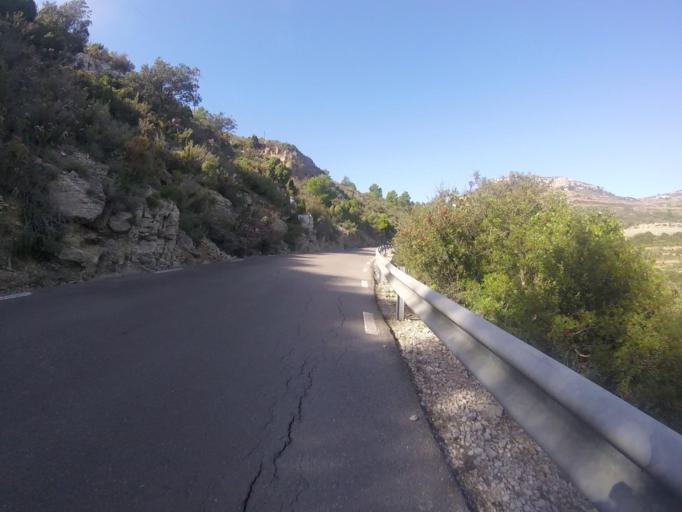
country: ES
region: Valencia
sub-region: Provincia de Castello
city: Sarratella
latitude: 40.2871
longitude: 0.0372
